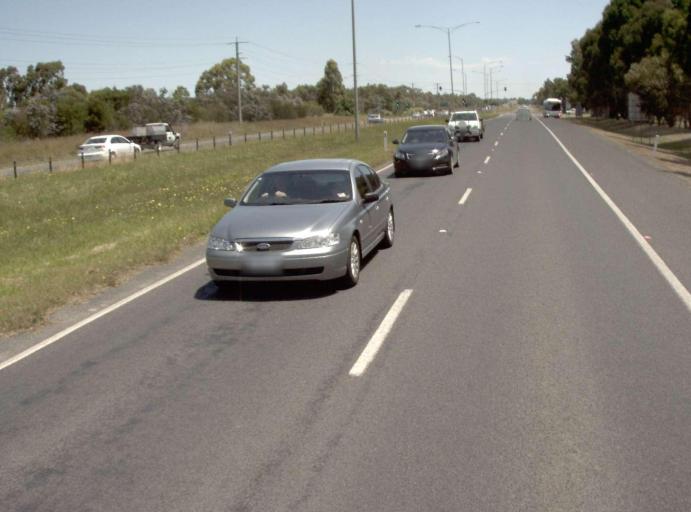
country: AU
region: Victoria
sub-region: Latrobe
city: Traralgon
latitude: -38.2193
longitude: 146.4736
